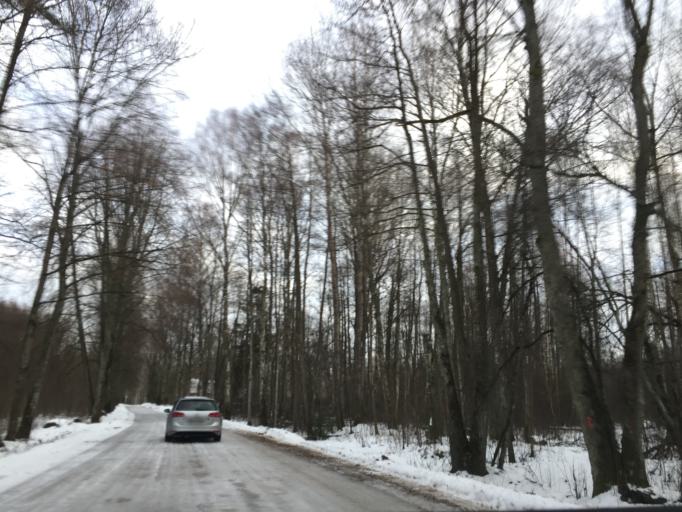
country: LV
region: Lielvarde
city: Lielvarde
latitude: 56.5799
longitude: 24.7768
